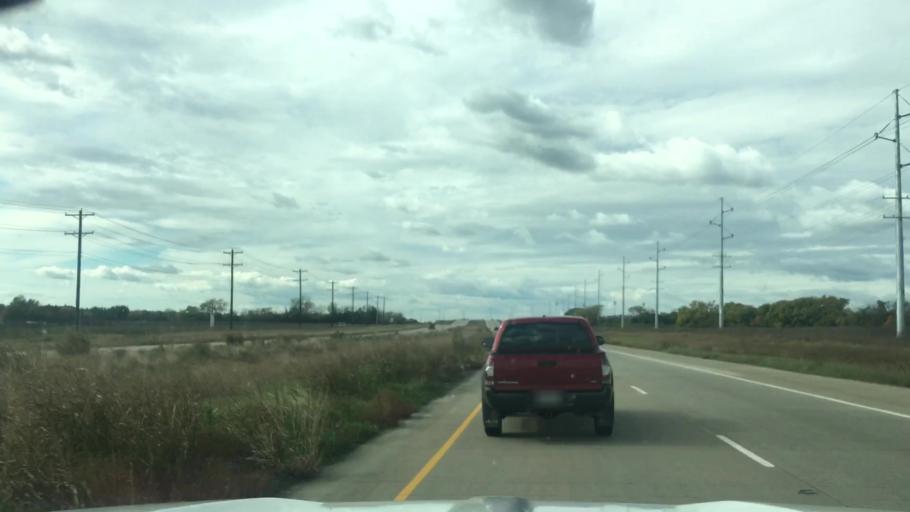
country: US
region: Texas
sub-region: Denton County
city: Denton
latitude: 33.2536
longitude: -97.1015
